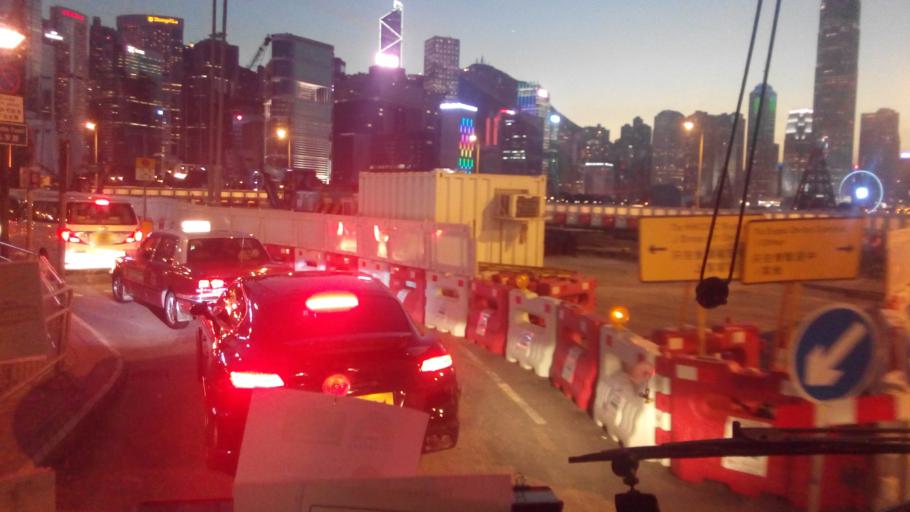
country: HK
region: Wanchai
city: Wan Chai
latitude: 22.2834
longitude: 114.1720
